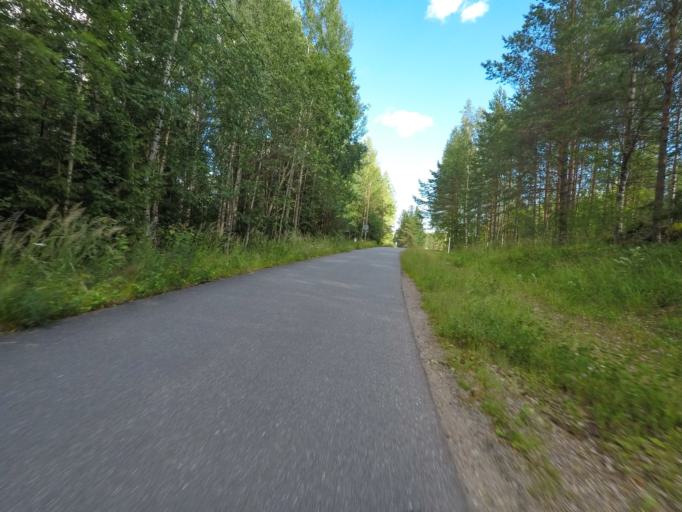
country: FI
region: South Karelia
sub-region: Lappeenranta
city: Lappeenranta
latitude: 61.1017
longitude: 28.1273
